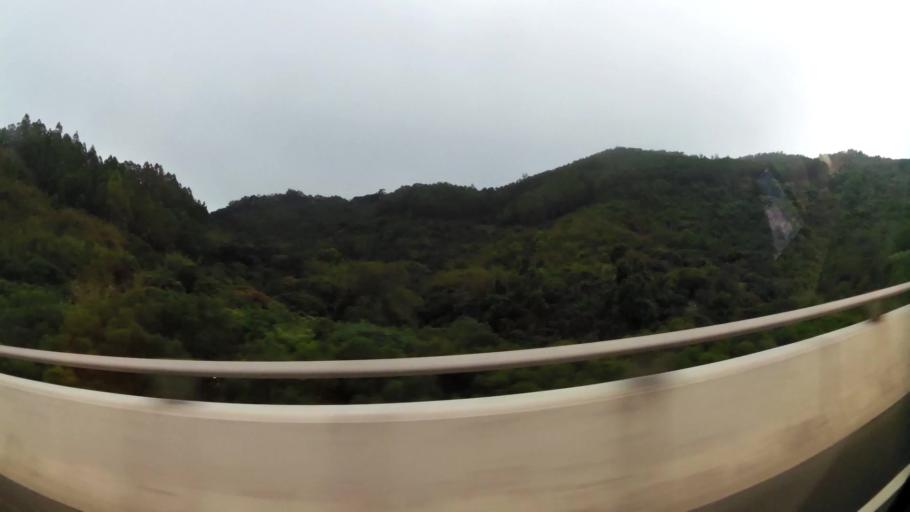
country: HK
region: Tsuen Wan
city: Tsuen Wan
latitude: 22.3603
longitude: 114.0916
